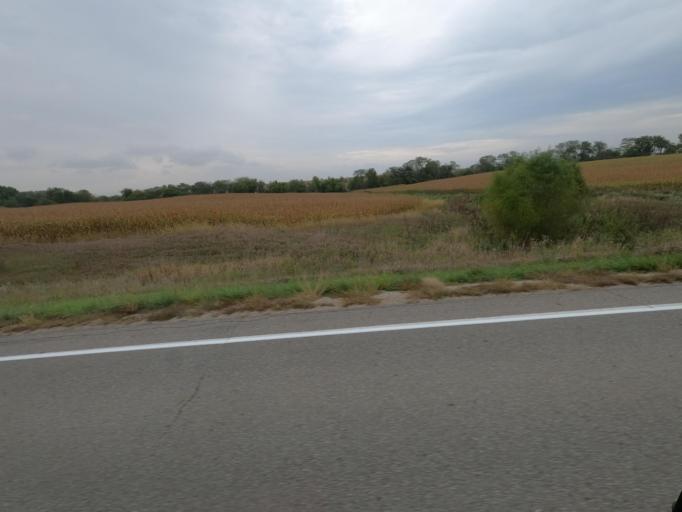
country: US
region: Iowa
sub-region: Van Buren County
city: Keosauqua
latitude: 40.8134
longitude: -91.8089
